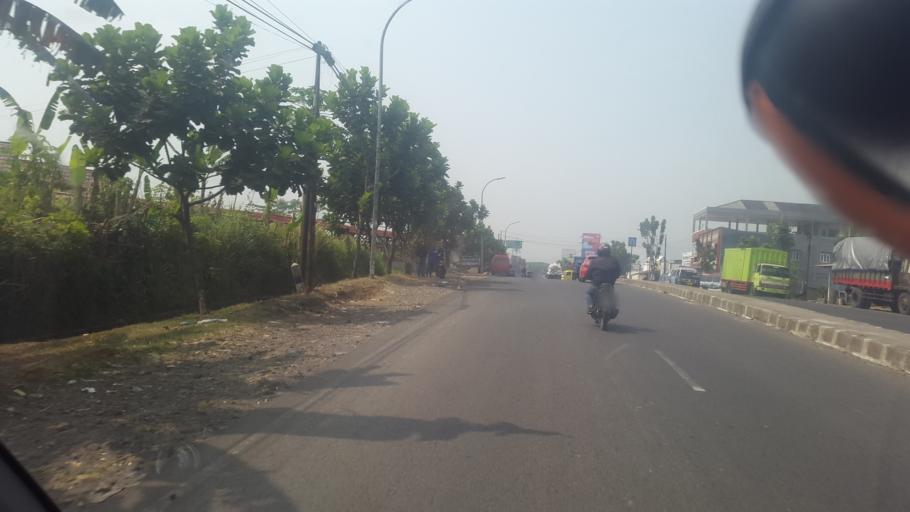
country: ID
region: West Java
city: Sukabumi
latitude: -6.9455
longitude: 106.9144
